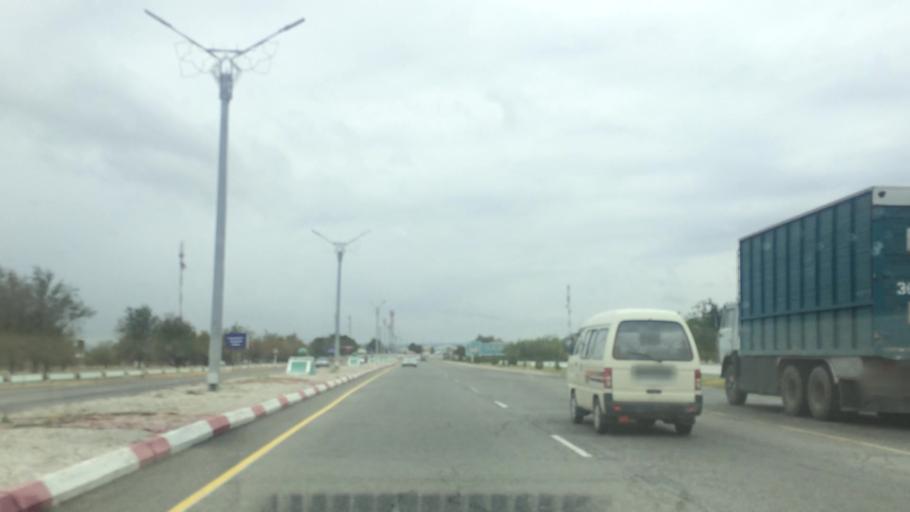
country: UZ
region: Samarqand
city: Bulung'ur
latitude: 39.8537
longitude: 67.4648
